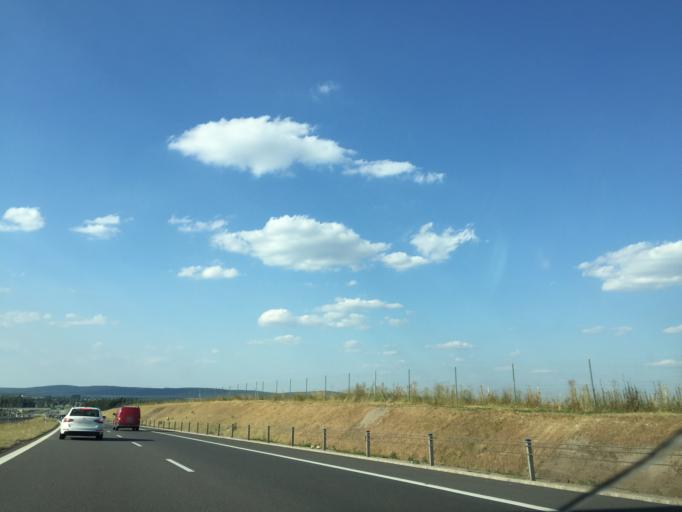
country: PL
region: Swietokrzyskie
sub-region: Powiat jedrzejowski
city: Sobkow
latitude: 50.7213
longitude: 20.4099
